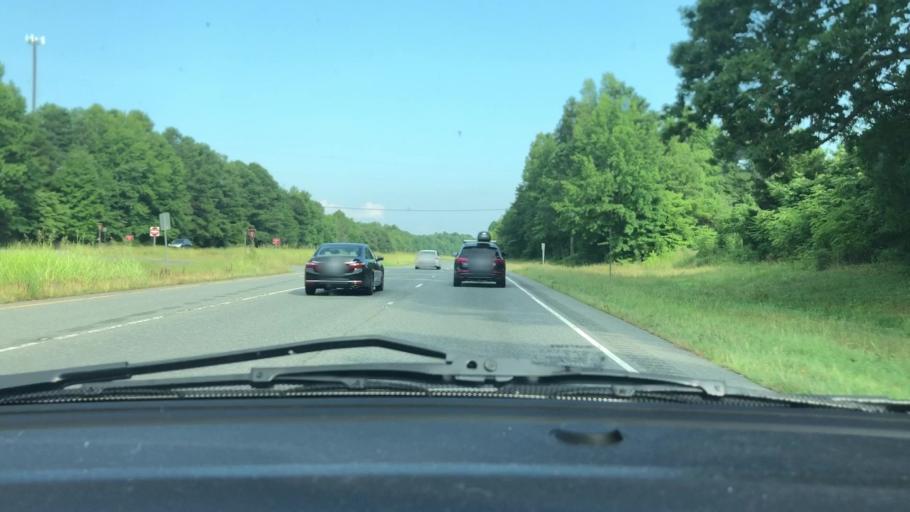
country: US
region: North Carolina
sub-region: Randolph County
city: Liberty
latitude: 35.8892
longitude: -79.6480
